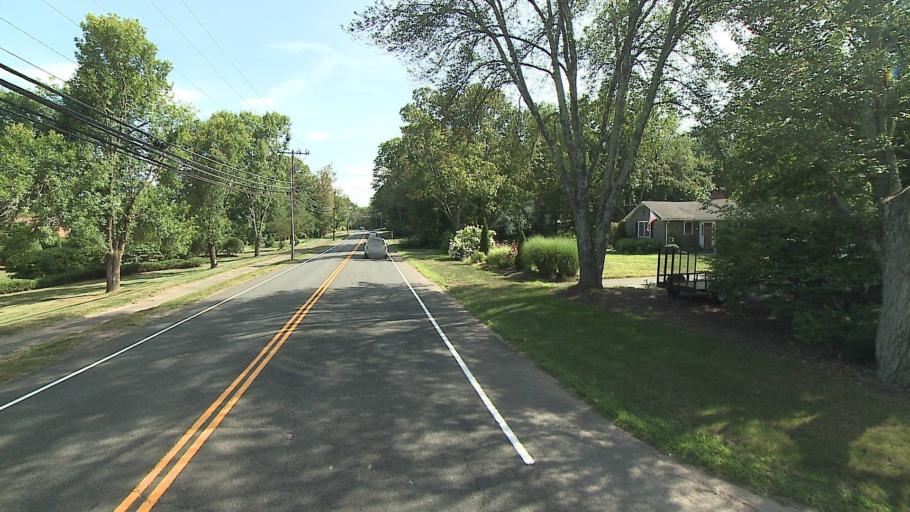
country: US
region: Connecticut
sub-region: Hartford County
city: Canton Valley
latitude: 41.7788
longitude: -72.8636
